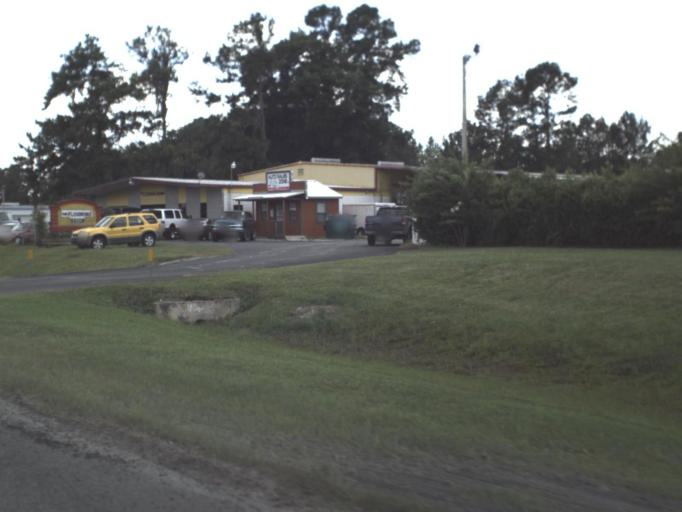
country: US
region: Florida
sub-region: Columbia County
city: Lake City
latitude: 30.1632
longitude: -82.6422
